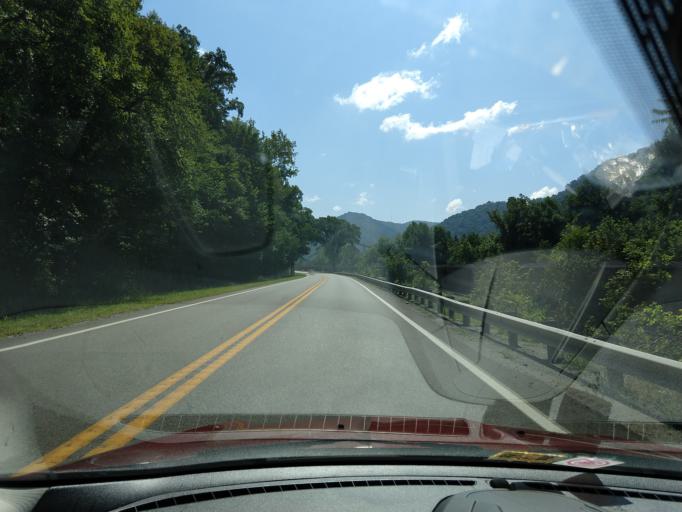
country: US
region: West Virginia
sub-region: Kanawha County
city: Montgomery
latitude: 38.1867
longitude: -81.3481
